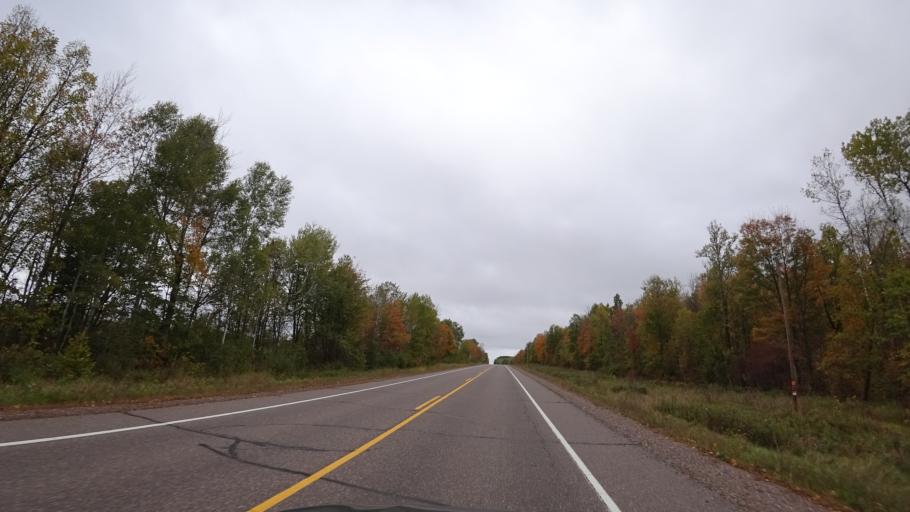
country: US
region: Wisconsin
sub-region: Rusk County
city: Ladysmith
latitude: 45.5684
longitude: -91.1116
